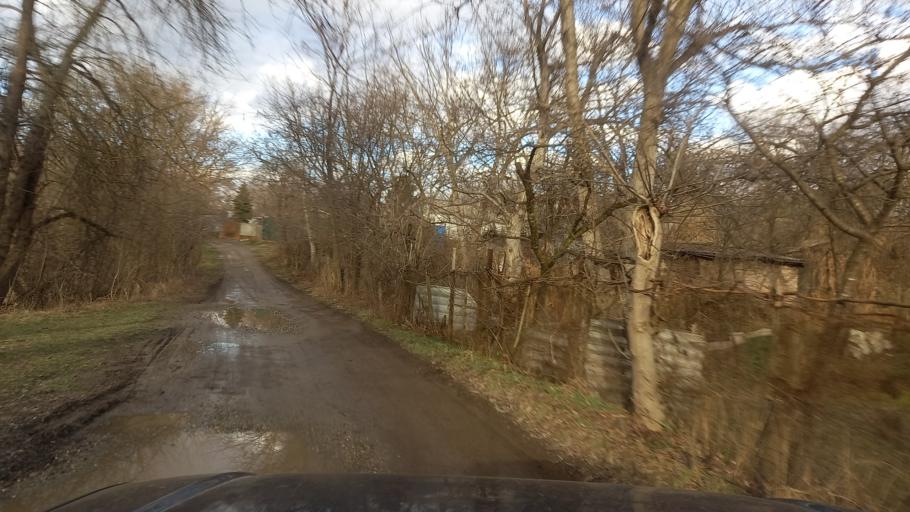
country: RU
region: Adygeya
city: Maykop
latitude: 44.5931
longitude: 40.0753
